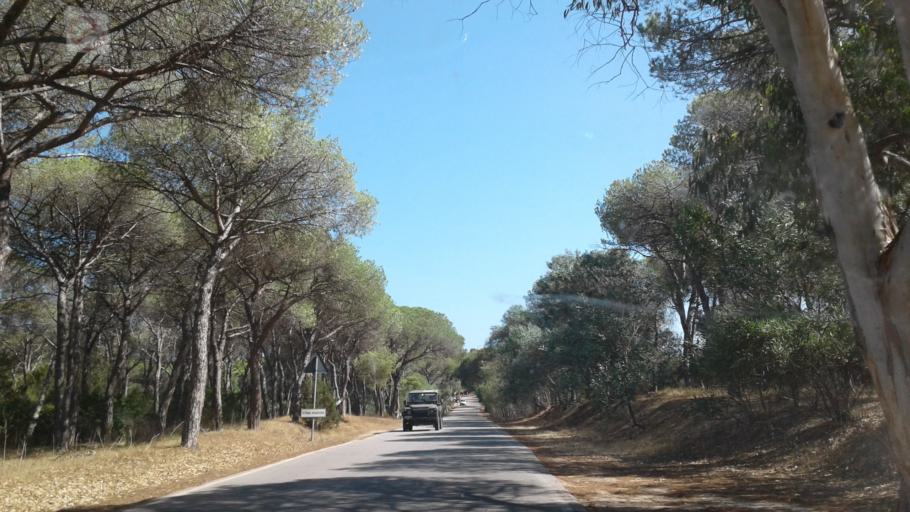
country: IT
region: Sardinia
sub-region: Provincia di Olbia-Tempio
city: La Maddalena
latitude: 41.2135
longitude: 9.4545
